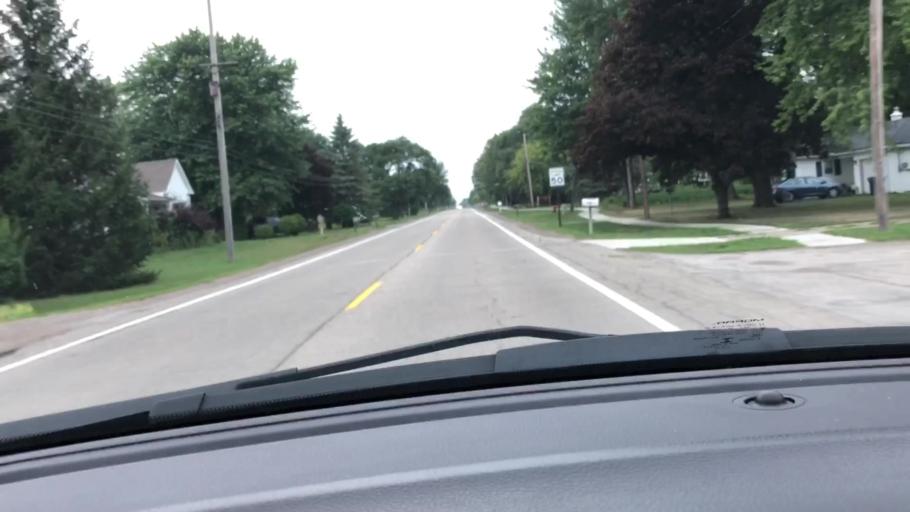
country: US
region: Michigan
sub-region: Bay County
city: Auburn
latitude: 43.6038
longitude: -84.1009
